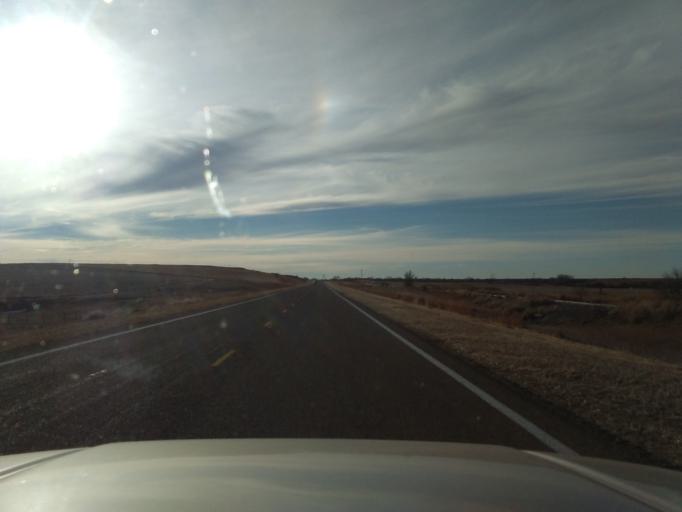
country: US
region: Kansas
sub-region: Norton County
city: Norton
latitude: 39.7495
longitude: -100.1476
